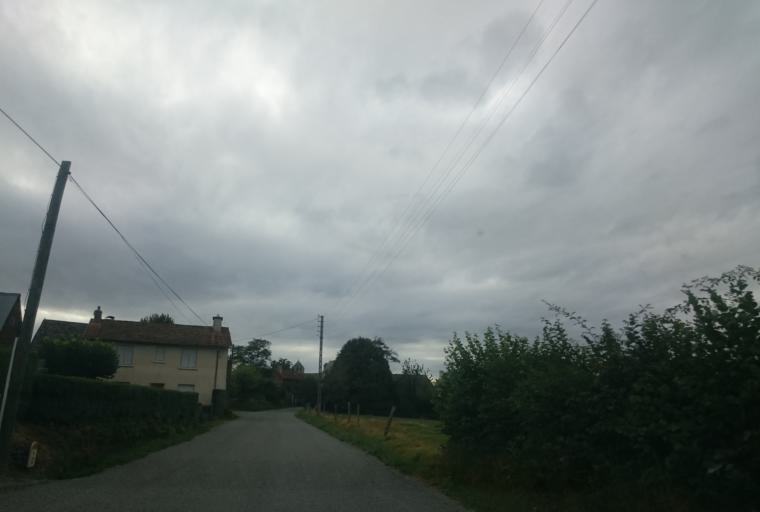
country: FR
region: Auvergne
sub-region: Departement du Cantal
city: Saint-Mamet-la-Salvetat
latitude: 44.8355
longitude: 2.3434
